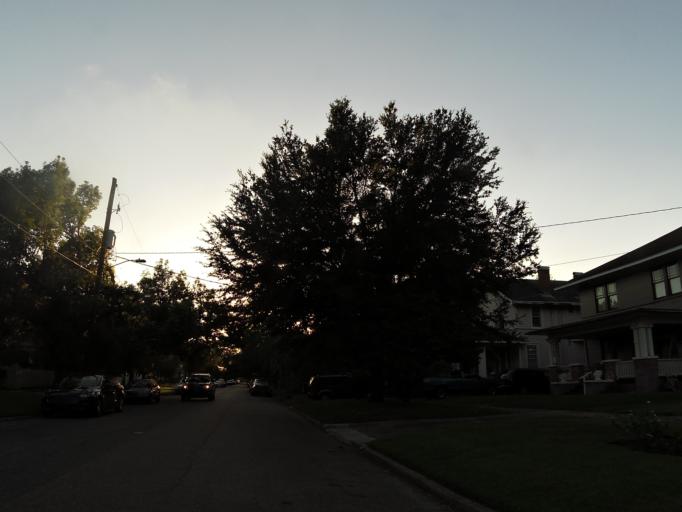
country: US
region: Florida
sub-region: Duval County
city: Jacksonville
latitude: 30.3168
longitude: -81.6851
